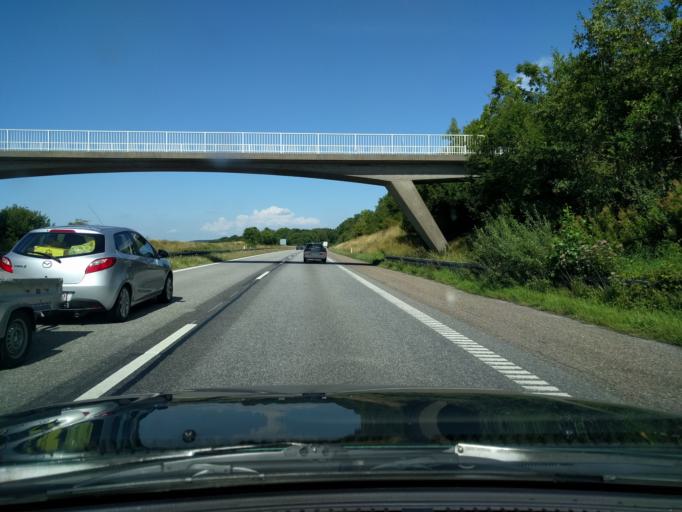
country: DK
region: Zealand
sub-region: Vordingborg Kommune
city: Nyrad
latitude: 55.0152
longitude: 11.9852
